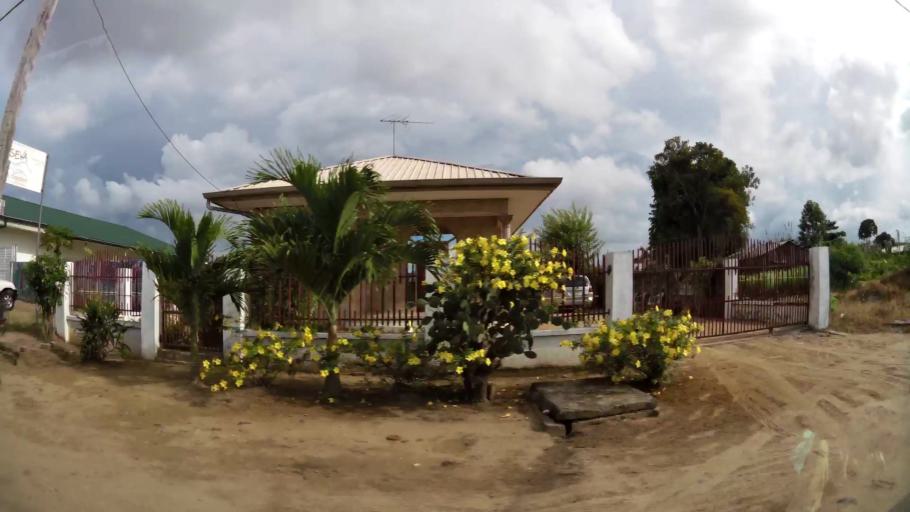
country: SR
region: Paramaribo
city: Paramaribo
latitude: 5.8579
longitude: -55.1812
